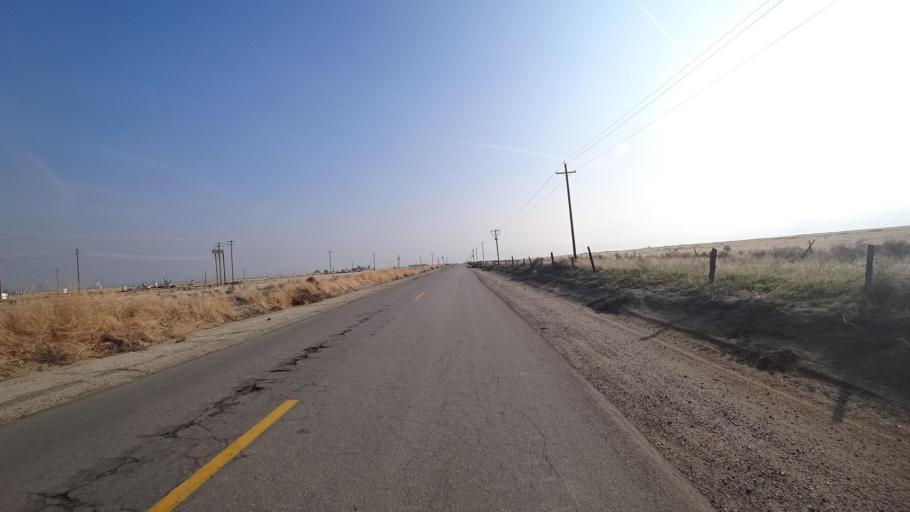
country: US
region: California
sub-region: Kern County
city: Lebec
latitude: 34.9845
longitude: -118.9240
